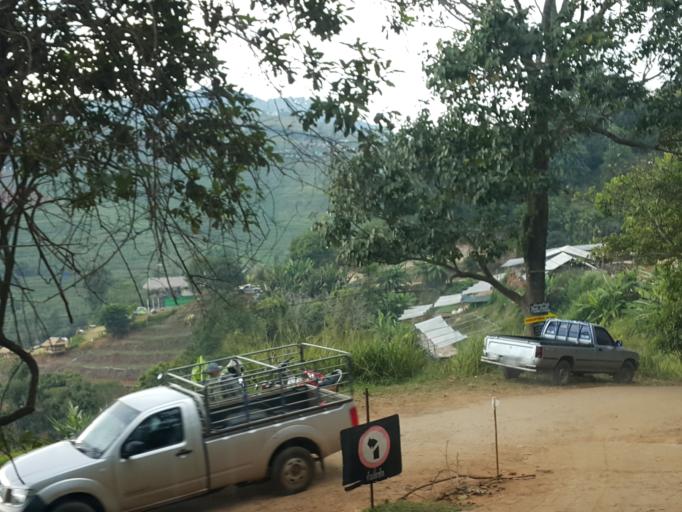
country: TH
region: Chiang Mai
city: Samoeng
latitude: 18.9342
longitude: 98.8225
